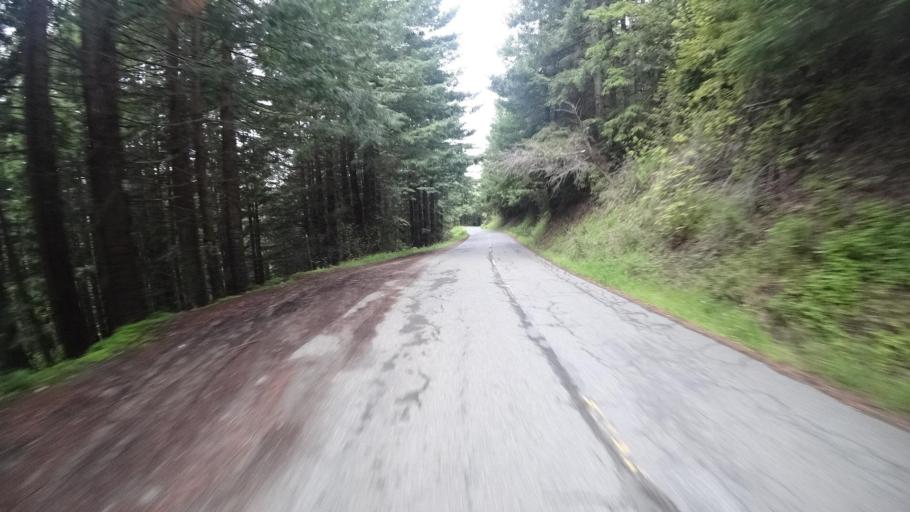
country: US
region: California
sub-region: Humboldt County
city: Blue Lake
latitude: 40.8729
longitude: -123.9734
